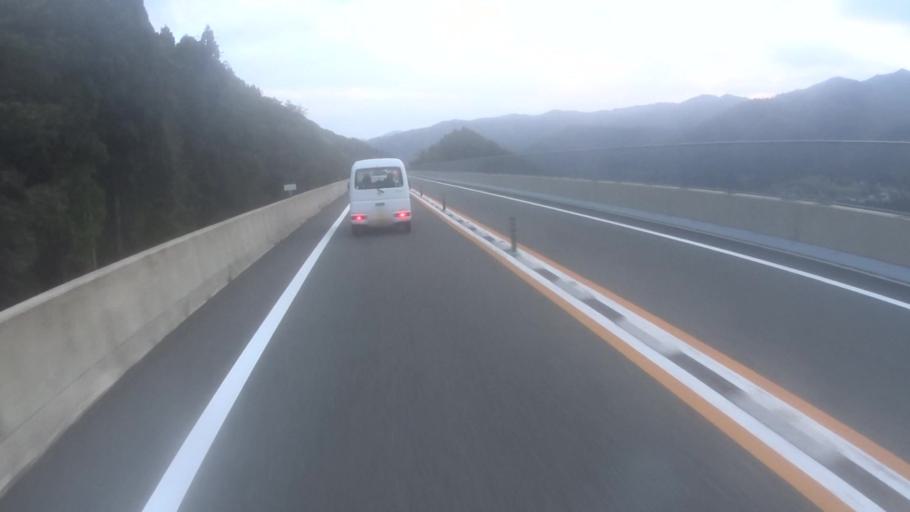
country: JP
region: Kyoto
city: Ayabe
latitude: 35.2881
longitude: 135.3364
